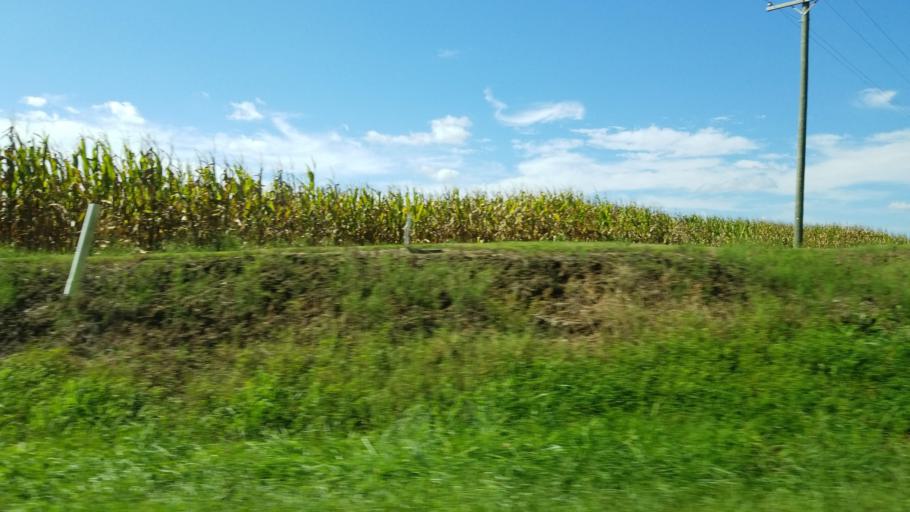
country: US
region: Illinois
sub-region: Williamson County
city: Marion
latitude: 37.7608
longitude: -88.8666
